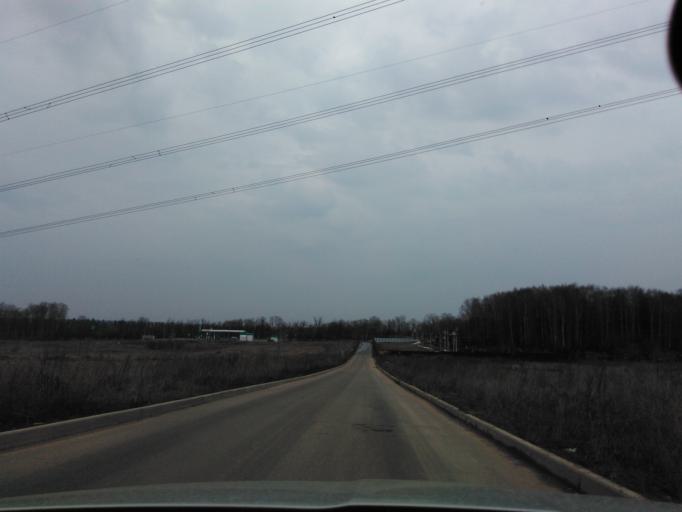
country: RU
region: Moskovskaya
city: Chashnikovo
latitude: 56.0360
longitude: 37.1523
